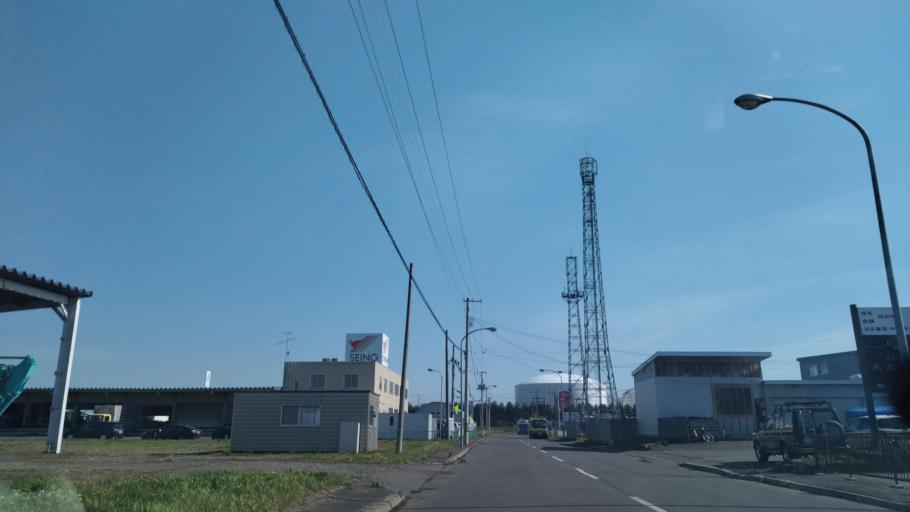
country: JP
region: Hokkaido
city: Obihiro
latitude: 42.9256
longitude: 143.0835
